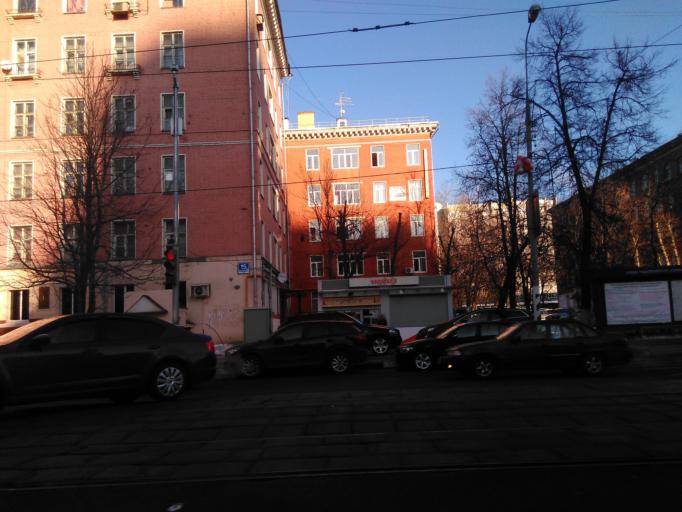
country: RU
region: Moskovskaya
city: Cheremushki
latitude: 55.6793
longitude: 37.5721
